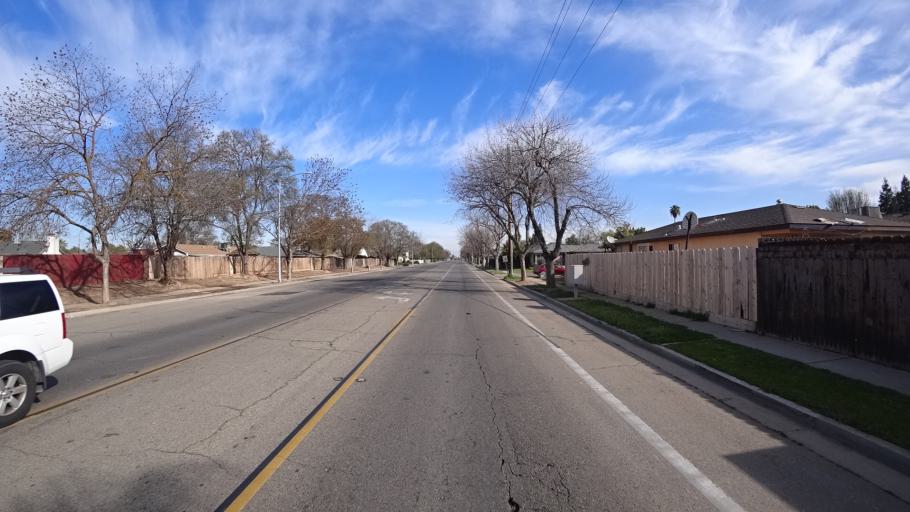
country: US
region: California
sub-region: Fresno County
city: West Park
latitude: 36.7952
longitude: -119.8804
